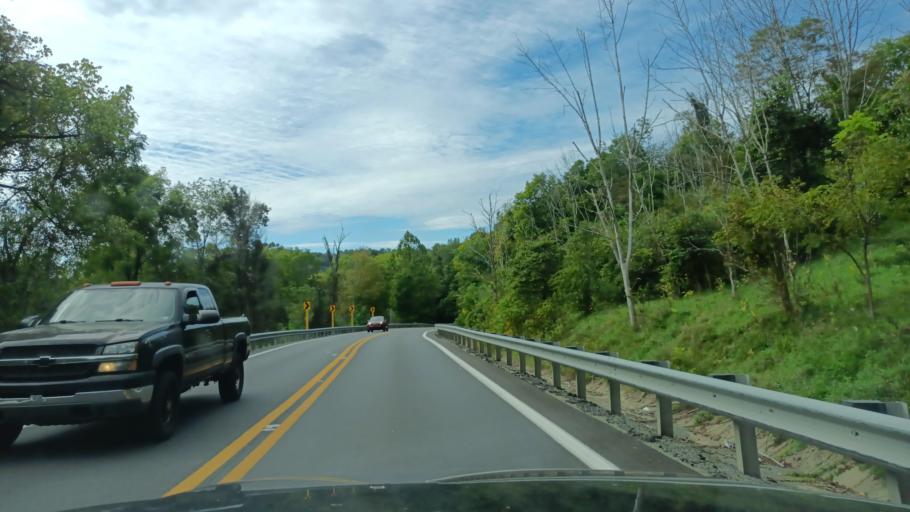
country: US
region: West Virginia
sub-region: Harrison County
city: Bridgeport
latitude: 39.3027
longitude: -80.1692
